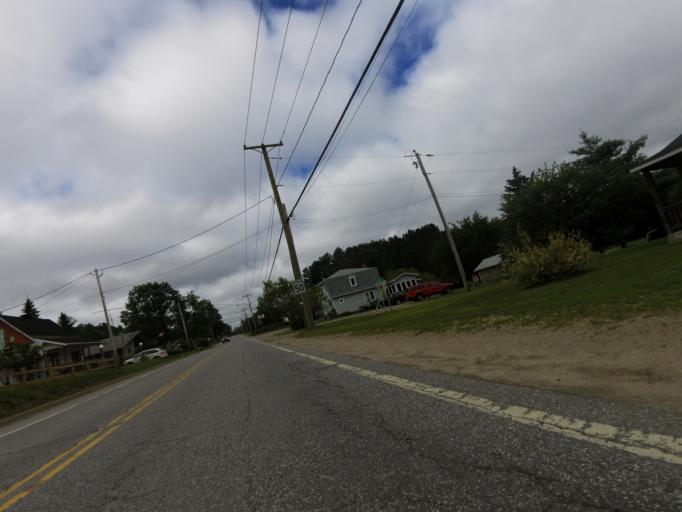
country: CA
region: Quebec
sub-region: Outaouais
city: Shawville
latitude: 45.8447
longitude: -76.4346
